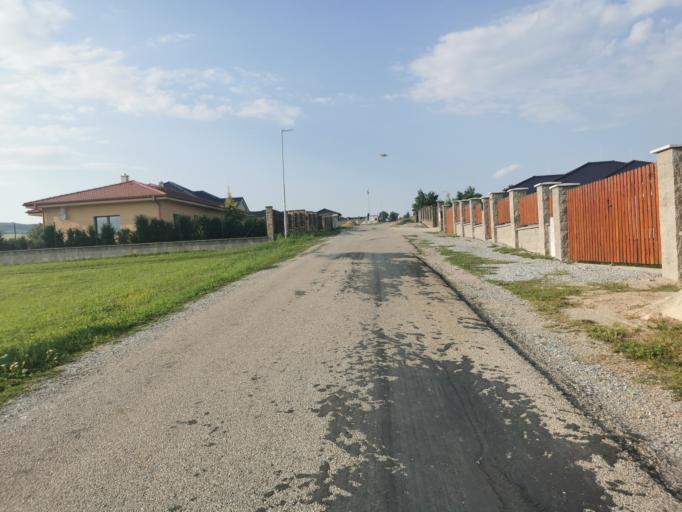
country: SK
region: Trenciansky
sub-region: Okres Myjava
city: Myjava
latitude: 48.7816
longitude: 17.5659
